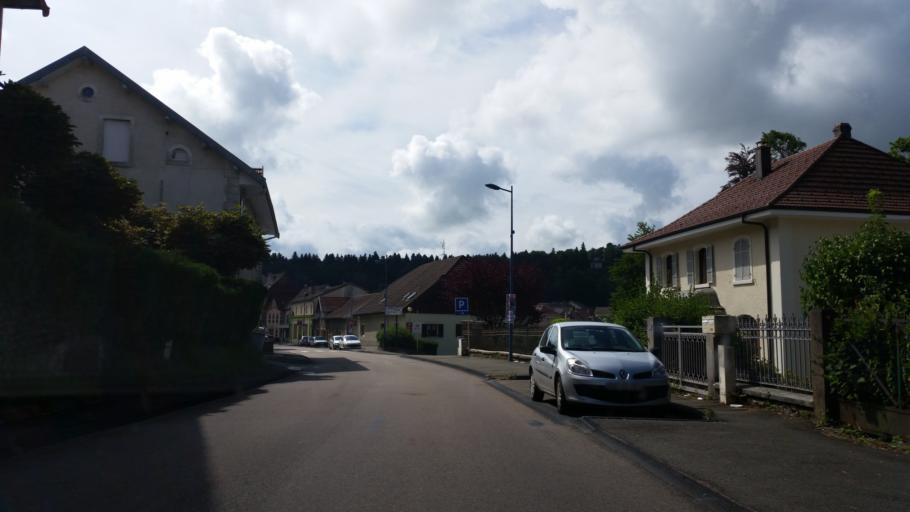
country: FR
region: Franche-Comte
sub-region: Departement du Doubs
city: Maiche
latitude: 47.2551
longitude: 6.8007
